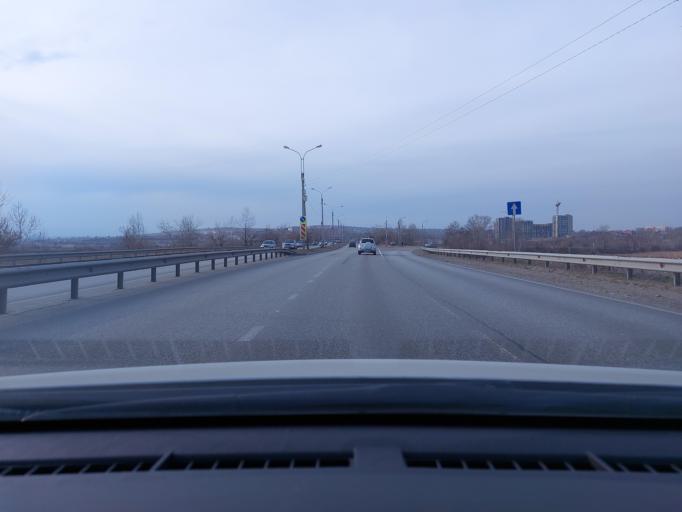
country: RU
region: Irkutsk
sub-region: Irkutskiy Rayon
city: Irkutsk
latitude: 52.3251
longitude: 104.2223
